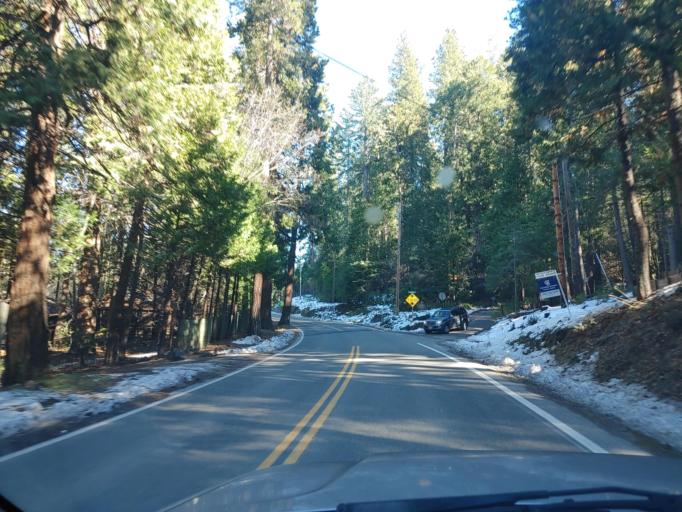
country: US
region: California
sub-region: Tuolumne County
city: Twain Harte
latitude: 38.0309
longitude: -120.2357
